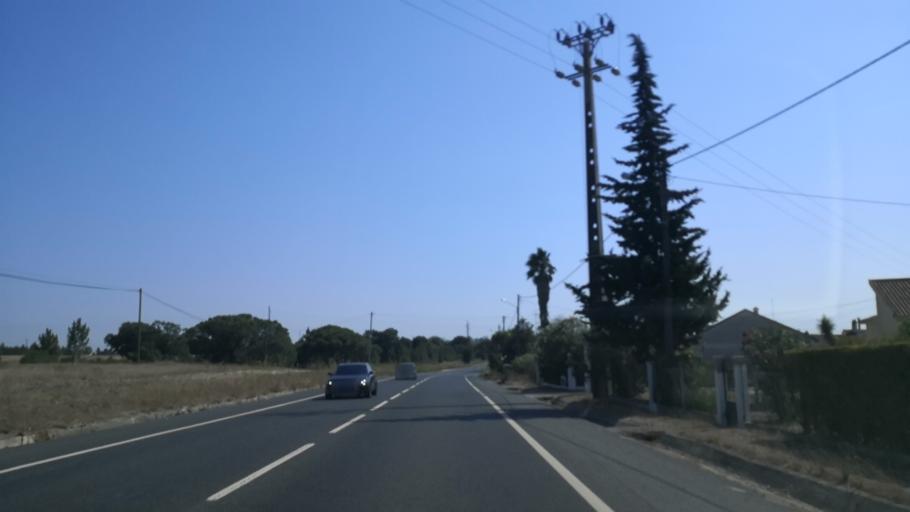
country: PT
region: Evora
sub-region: Vendas Novas
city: Vendas Novas
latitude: 38.6925
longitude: -8.6122
